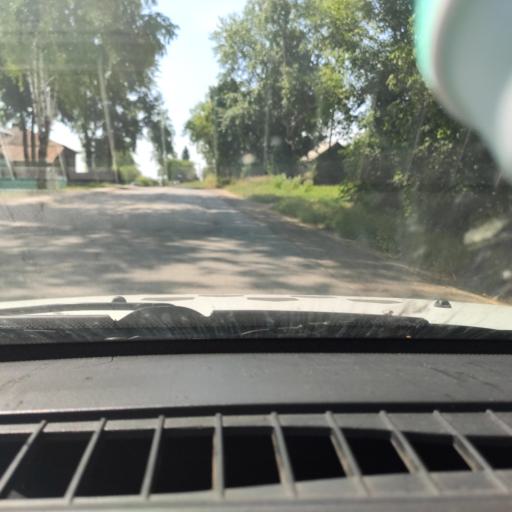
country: RU
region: Perm
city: Okhansk
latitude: 57.7208
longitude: 55.3764
